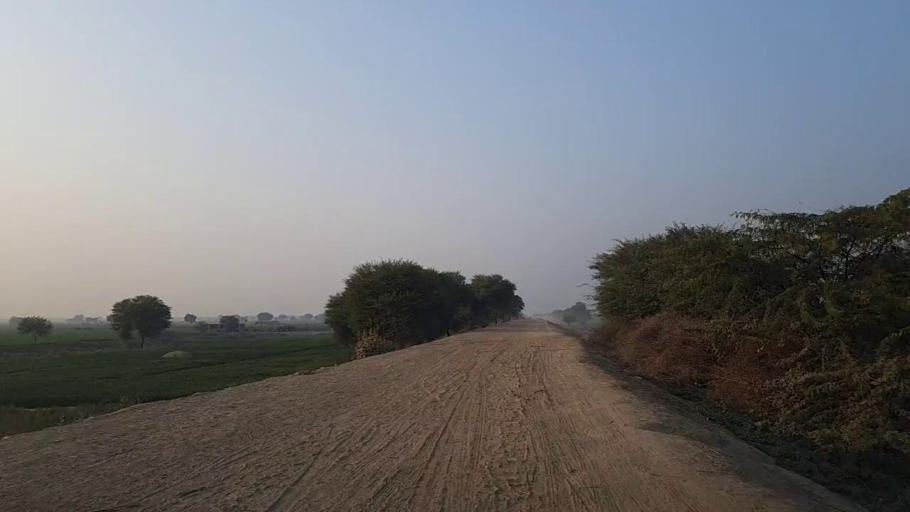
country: PK
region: Sindh
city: Sann
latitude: 26.1805
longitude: 68.0953
